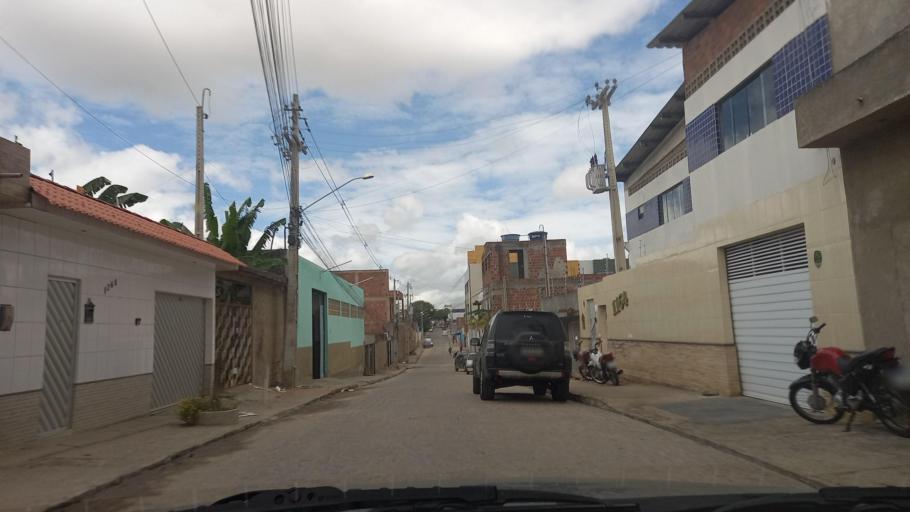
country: BR
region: Pernambuco
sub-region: Caruaru
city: Caruaru
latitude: -8.2683
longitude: -35.9588
